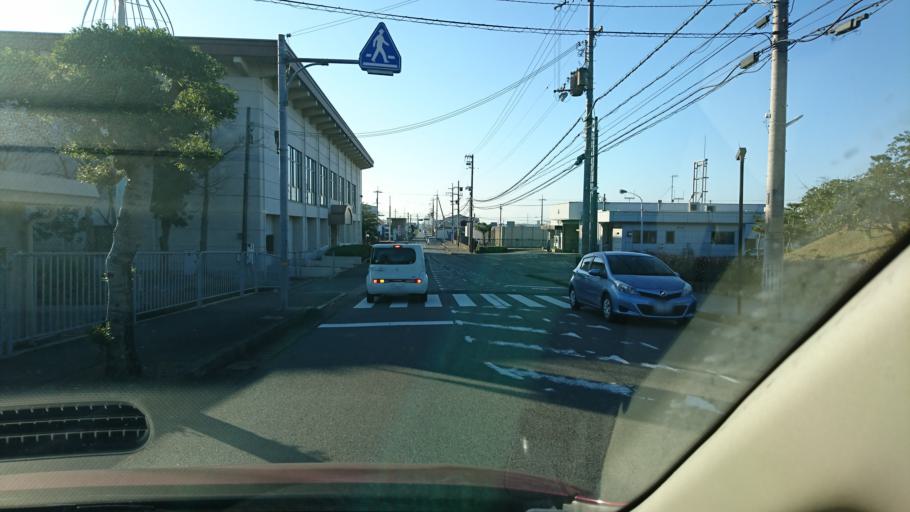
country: JP
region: Hyogo
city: Miki
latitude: 34.7488
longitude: 134.9210
